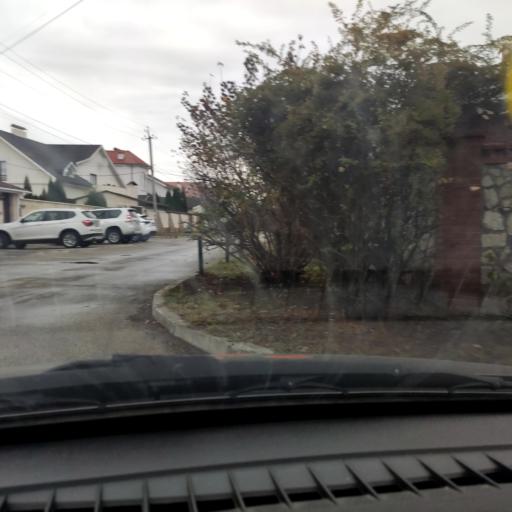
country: RU
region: Samara
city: Tol'yatti
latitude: 53.5428
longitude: 49.3736
